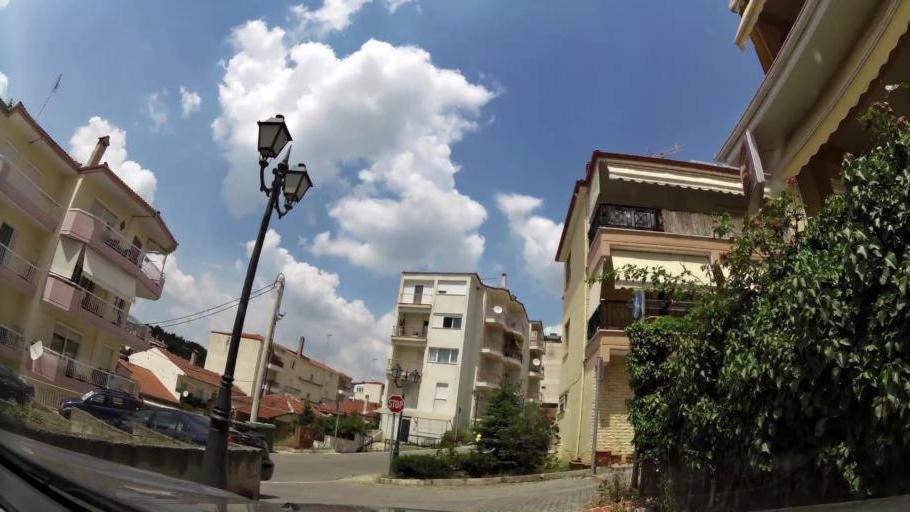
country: GR
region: West Macedonia
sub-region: Nomos Kozanis
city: Kozani
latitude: 40.3079
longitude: 21.7920
